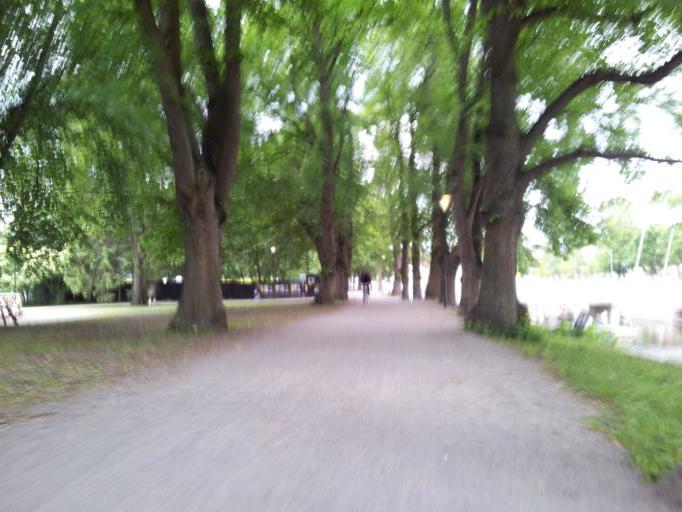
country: SE
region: Uppsala
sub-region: Uppsala Kommun
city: Uppsala
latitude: 59.8508
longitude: 17.6458
